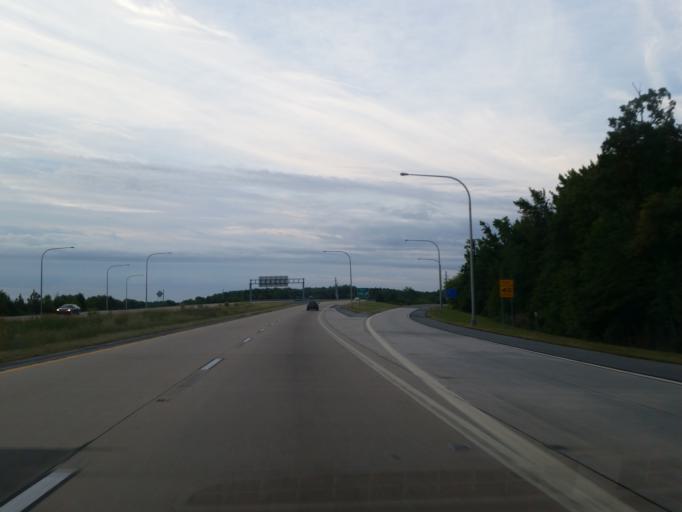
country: US
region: Delaware
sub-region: Kent County
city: Dover
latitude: 39.1708
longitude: -75.4957
